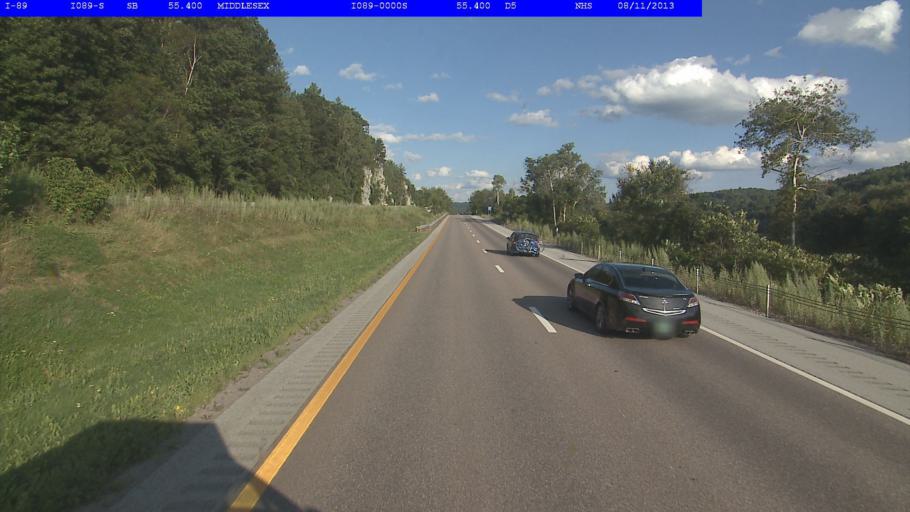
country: US
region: Vermont
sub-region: Washington County
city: Montpelier
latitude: 44.2707
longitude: -72.6333
